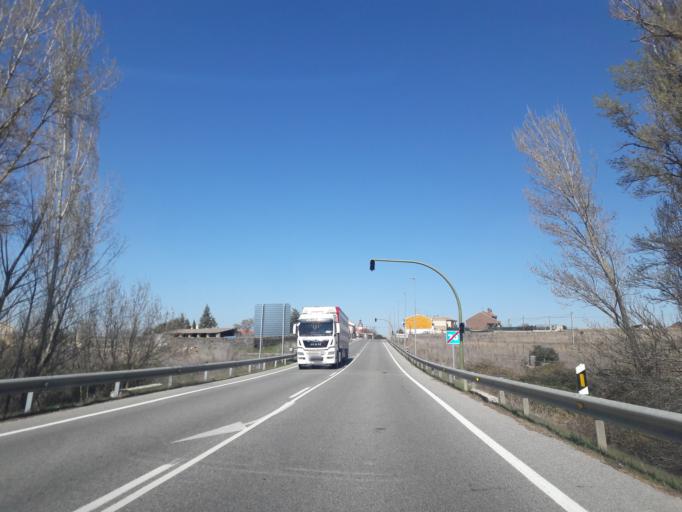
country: ES
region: Castille and Leon
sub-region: Provincia de Salamanca
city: Mozarbez
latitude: 40.8539
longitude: -5.6487
